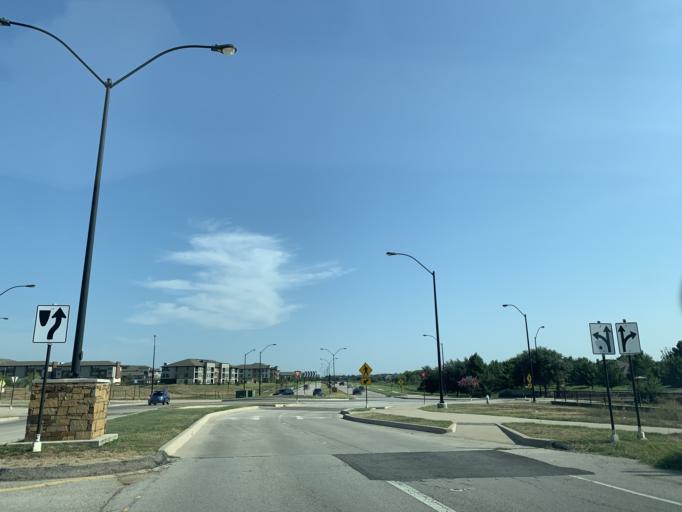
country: US
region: Texas
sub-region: Tarrant County
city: Blue Mound
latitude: 32.9029
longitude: -97.3070
